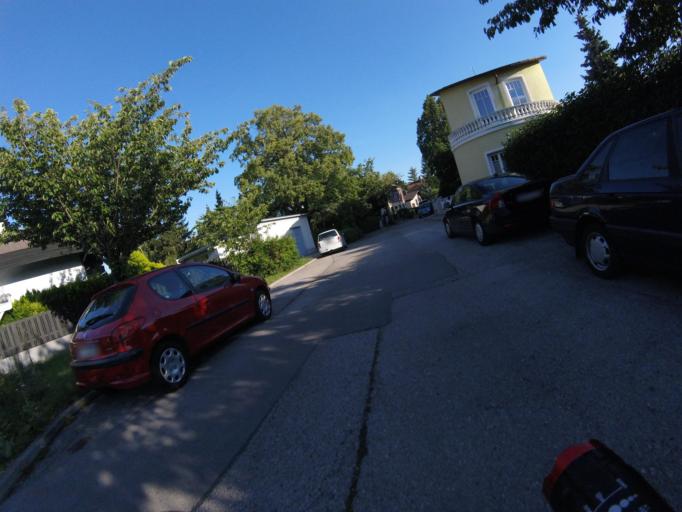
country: AT
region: Lower Austria
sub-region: Politischer Bezirk Modling
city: Modling
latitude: 48.0761
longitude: 16.2989
